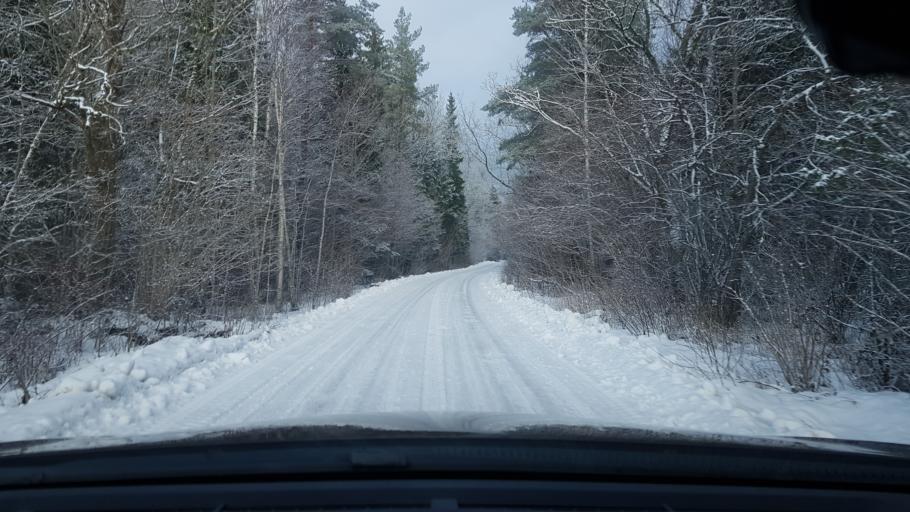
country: EE
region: Harju
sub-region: Keila linn
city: Keila
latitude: 59.2870
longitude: 24.2603
